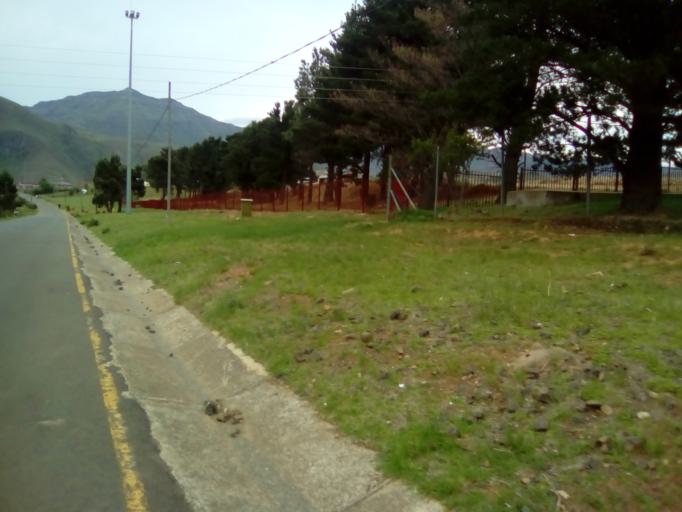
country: LS
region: Qacha's Nek
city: Qacha's Nek
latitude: -30.1117
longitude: 28.6812
